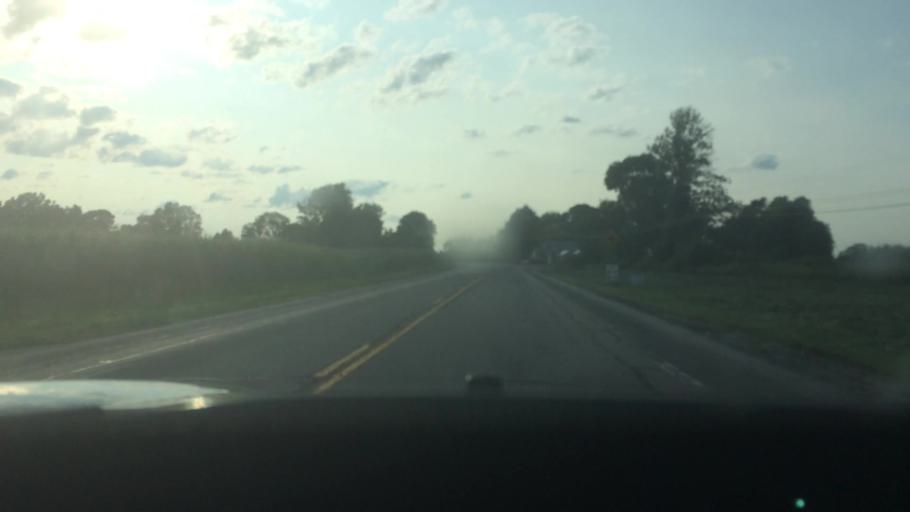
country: US
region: New York
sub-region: St. Lawrence County
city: Ogdensburg
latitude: 44.6704
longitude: -75.3824
